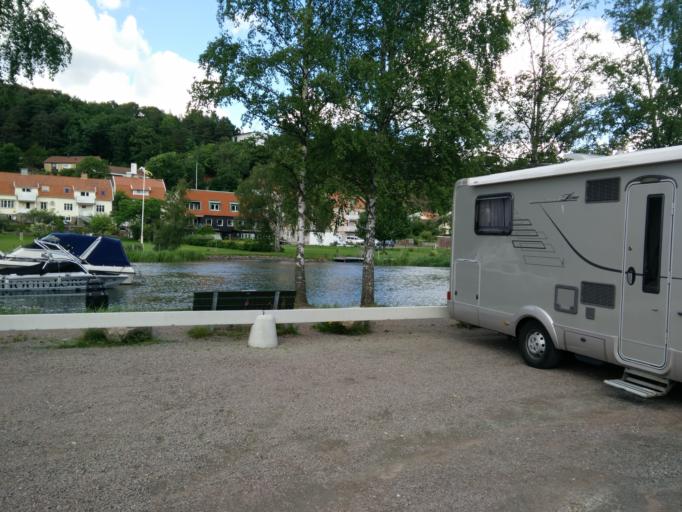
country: SE
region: Vaestra Goetaland
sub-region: Kungalvs Kommun
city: Kungalv
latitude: 57.8638
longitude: 11.9983
